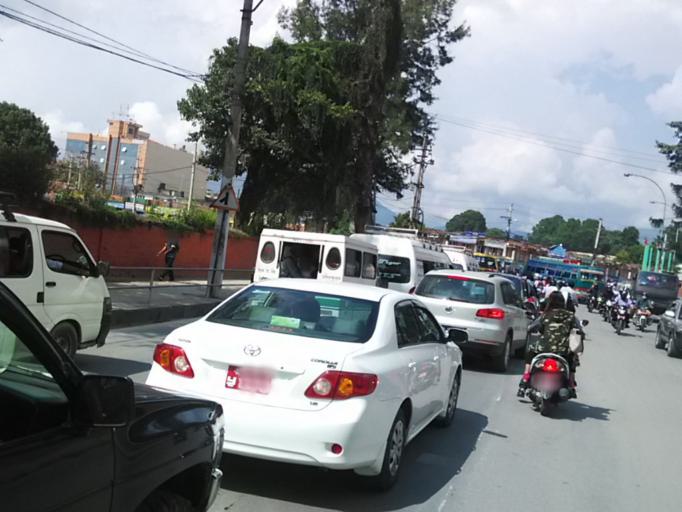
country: NP
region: Central Region
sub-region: Bagmati Zone
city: Kathmandu
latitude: 27.7162
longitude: 85.3159
